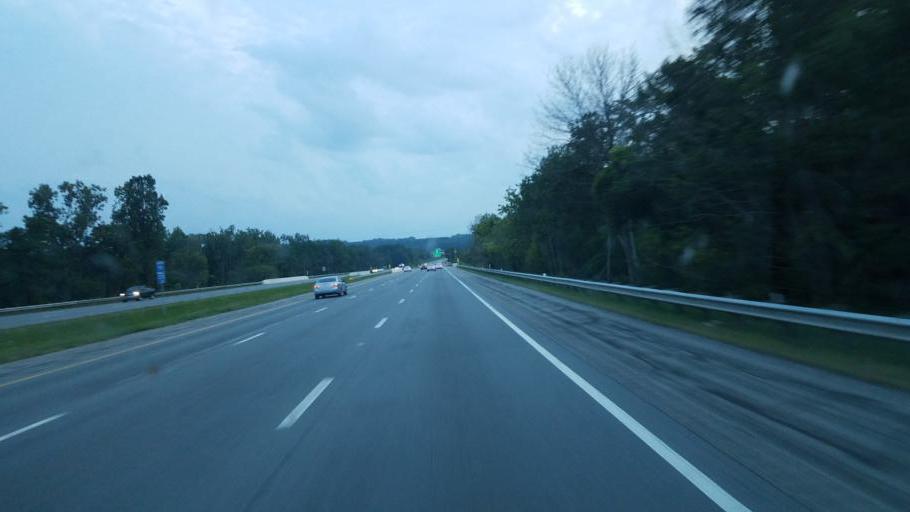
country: US
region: Ohio
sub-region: Richland County
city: Lincoln Heights
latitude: 40.7453
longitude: -82.4493
